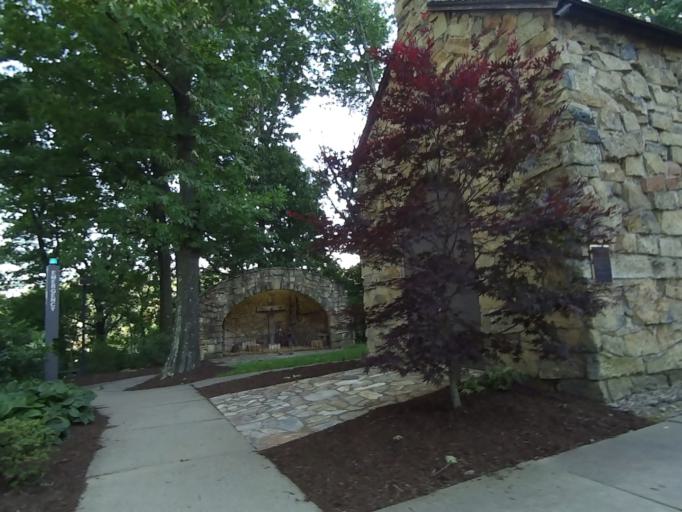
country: US
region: Ohio
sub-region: Jefferson County
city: Steubenville
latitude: 40.3756
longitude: -80.6201
